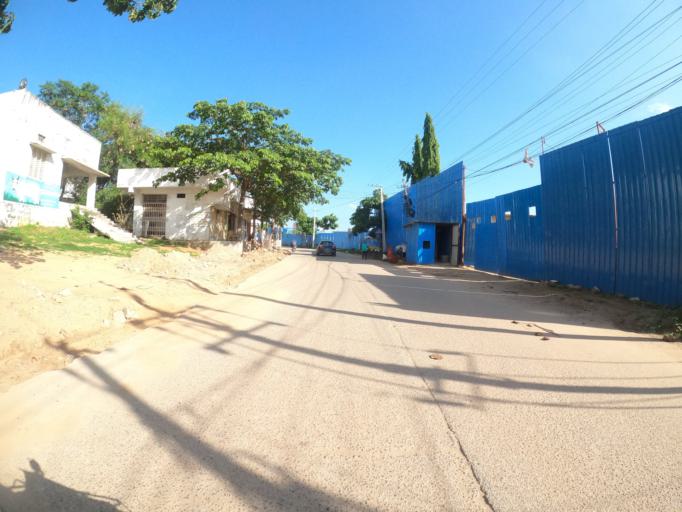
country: IN
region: Telangana
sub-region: Hyderabad
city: Hyderabad
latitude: 17.3564
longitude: 78.3764
